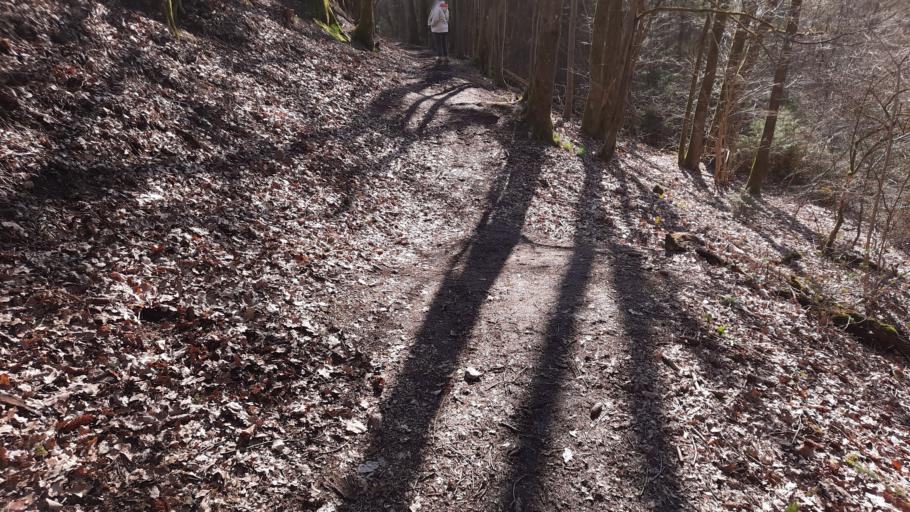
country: BE
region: Wallonia
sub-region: Province du Luxembourg
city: Houffalize
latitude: 50.1366
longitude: 5.8021
